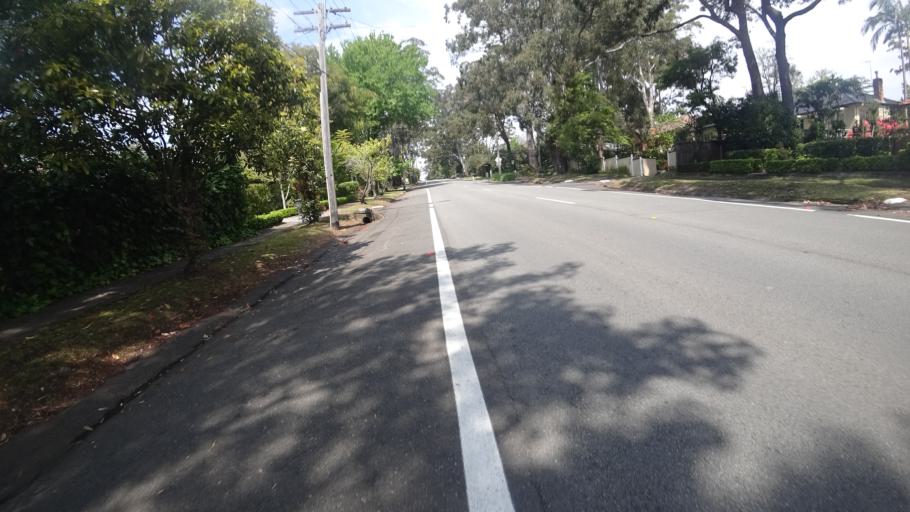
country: AU
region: New South Wales
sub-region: City of Sydney
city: North Turramurra
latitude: -33.7238
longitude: 151.1397
